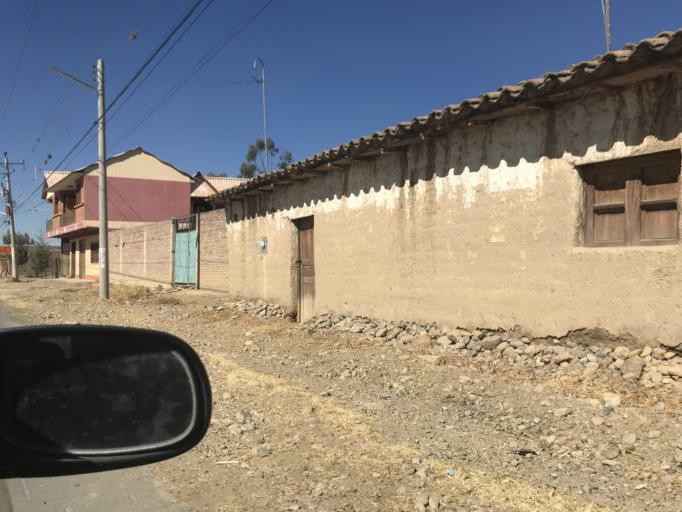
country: BO
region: Cochabamba
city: Tarata
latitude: -17.6033
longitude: -65.9858
